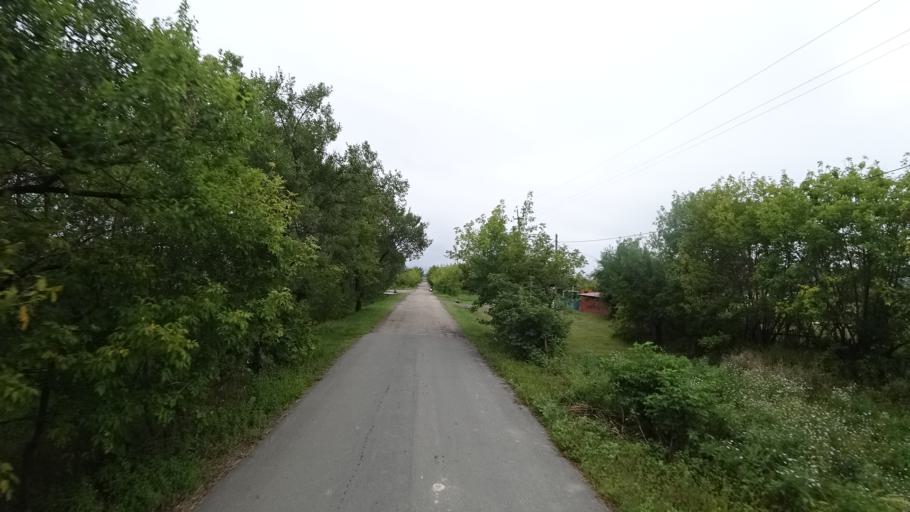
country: RU
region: Primorskiy
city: Chernigovka
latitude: 44.3288
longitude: 132.5969
